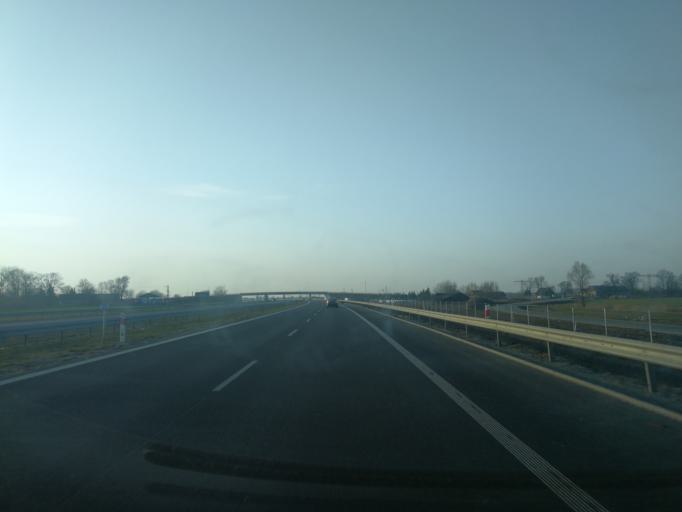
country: PL
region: Pomeranian Voivodeship
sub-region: Powiat nowodworski
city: Ostaszewo
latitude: 54.2494
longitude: 18.9874
